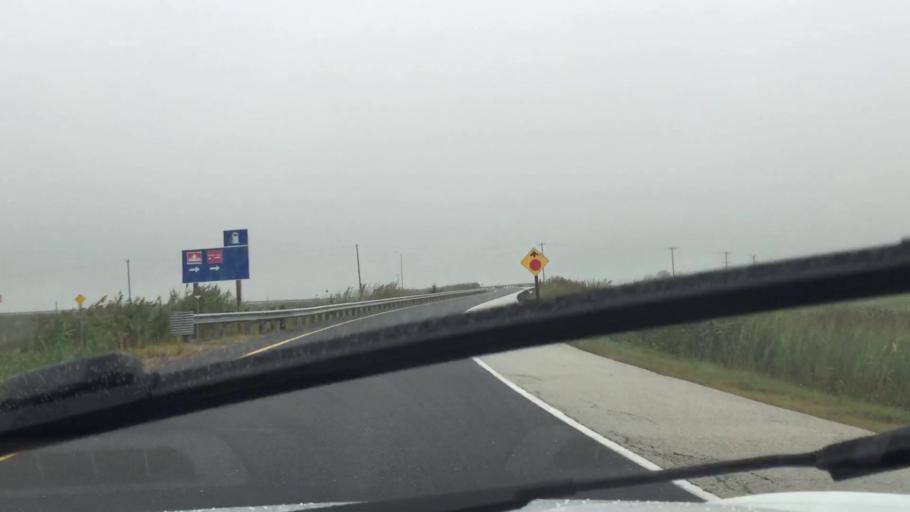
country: CA
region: Ontario
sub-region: Lambton County
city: Walpole Island
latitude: 42.2420
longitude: -82.5550
